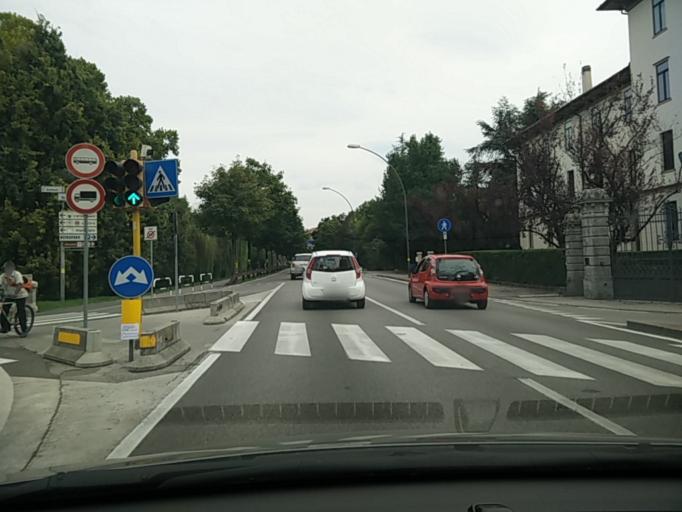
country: IT
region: Veneto
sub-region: Provincia di Treviso
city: Treviso
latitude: 45.6637
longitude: 12.2361
